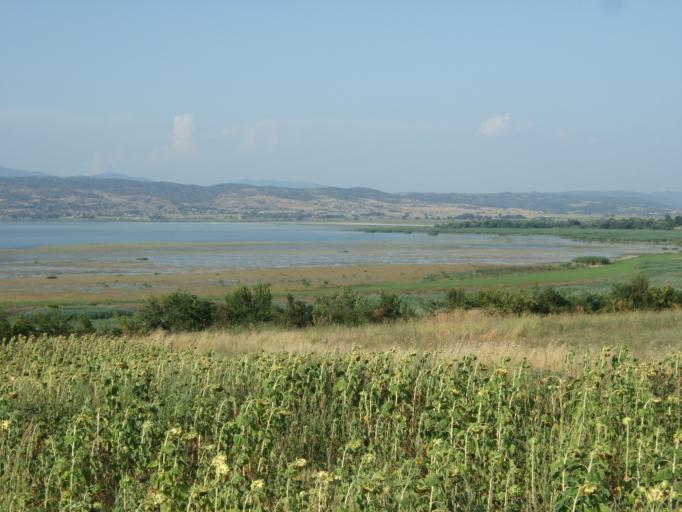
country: GR
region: Central Macedonia
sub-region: Nomos Thessalonikis
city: Agios Vasileios
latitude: 40.6516
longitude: 23.1665
